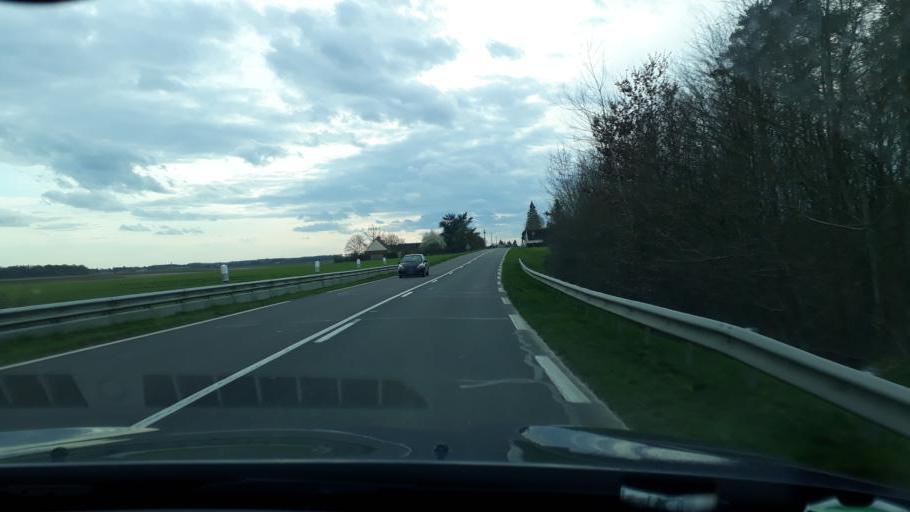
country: FR
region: Centre
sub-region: Departement du Loiret
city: Loury
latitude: 48.0190
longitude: 2.1134
